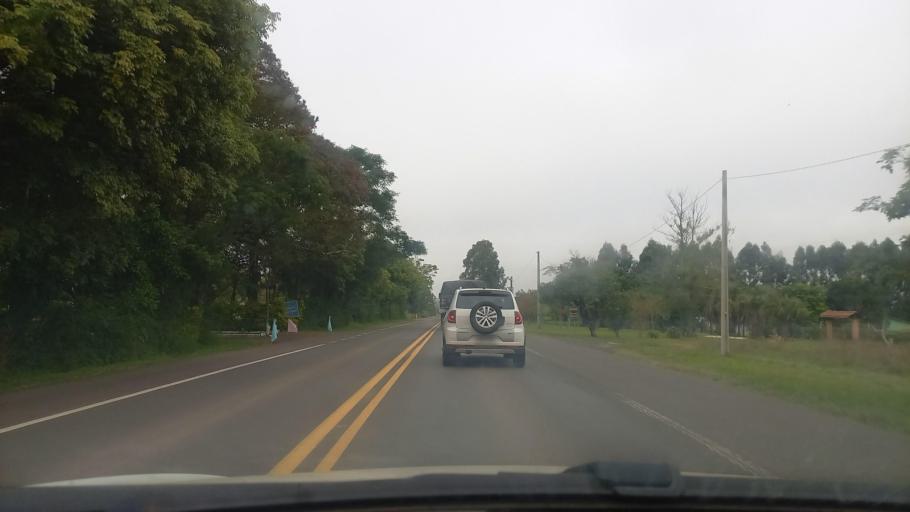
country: BR
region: Rio Grande do Sul
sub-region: Rosario Do Sul
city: Rosario do Sul
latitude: -30.2716
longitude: -54.9765
